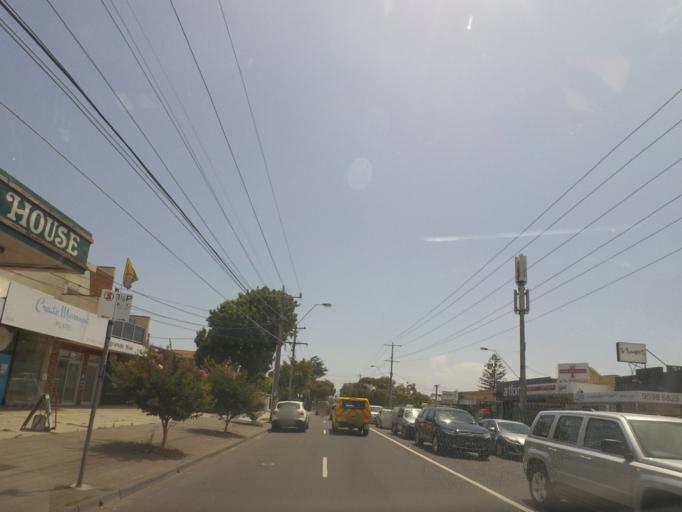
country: AU
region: Victoria
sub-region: Bayside
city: Hampton East
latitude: -37.9534
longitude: 145.0207
